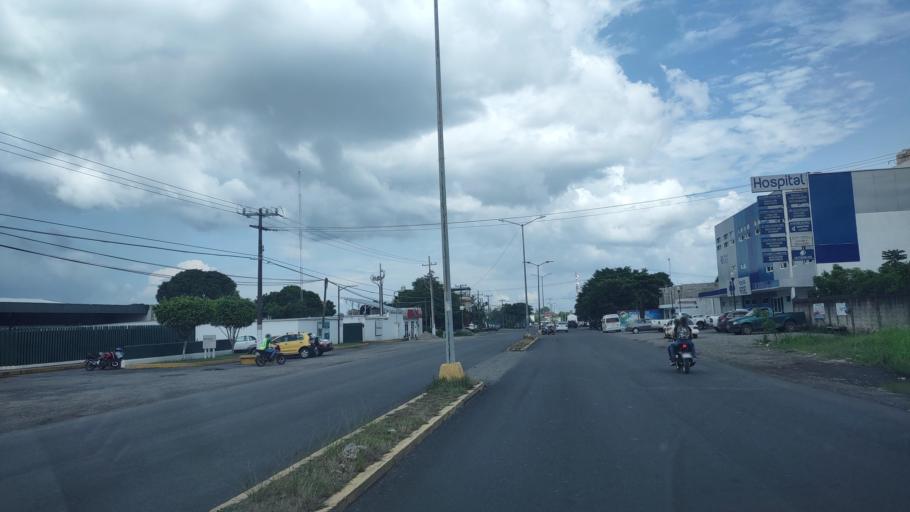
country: MX
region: Veracruz
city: Martinez de la Torre
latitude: 20.0704
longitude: -97.0699
